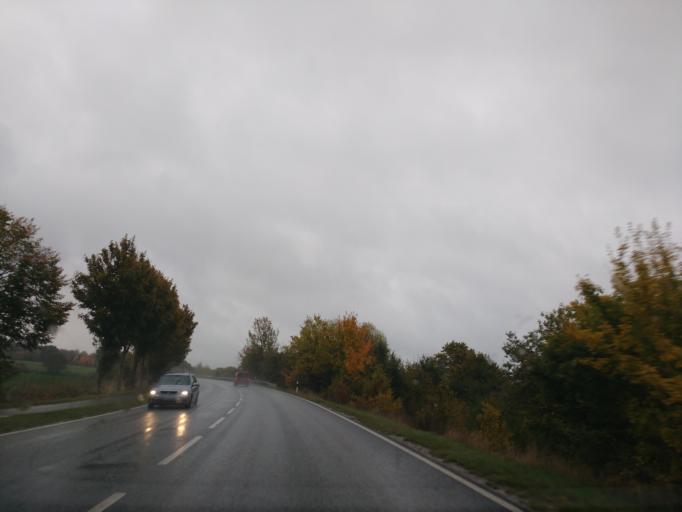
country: DE
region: Schleswig-Holstein
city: Eutin
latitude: 54.1173
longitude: 10.6450
